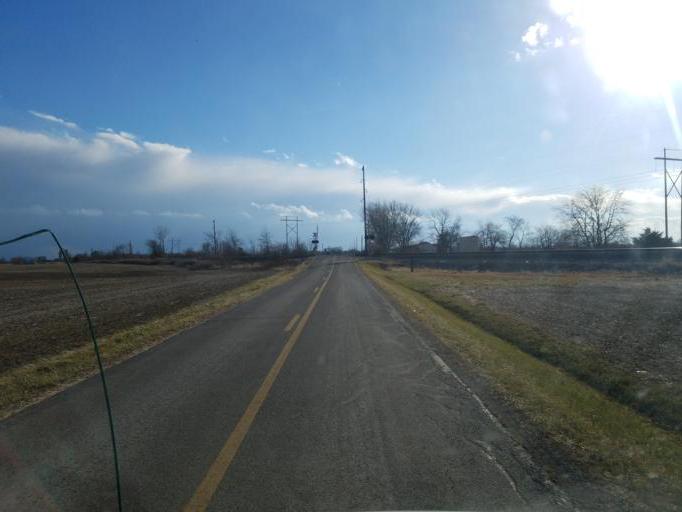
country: US
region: Ohio
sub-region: Marion County
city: Prospect
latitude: 40.4021
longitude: -83.1444
